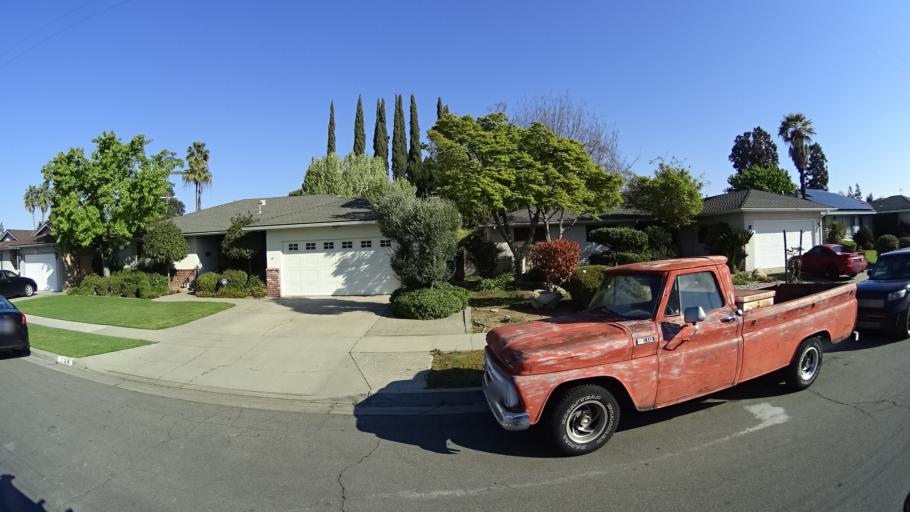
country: US
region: California
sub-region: Fresno County
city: Clovis
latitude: 36.8276
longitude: -119.7782
